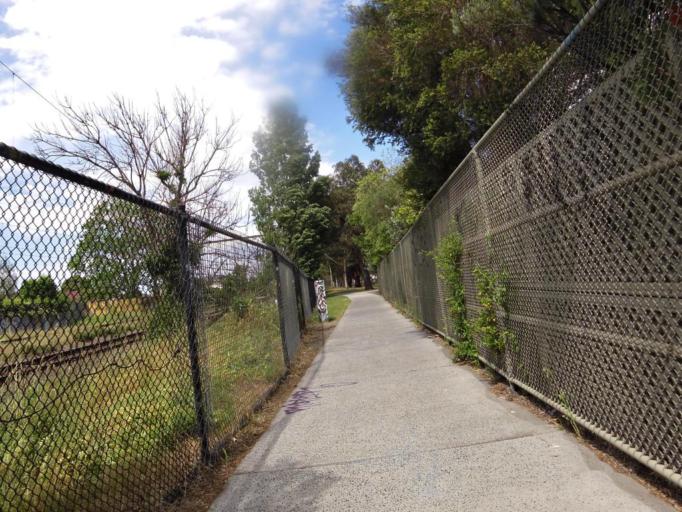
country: AU
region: Victoria
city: Hughesdale
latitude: -37.8955
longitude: 145.0786
